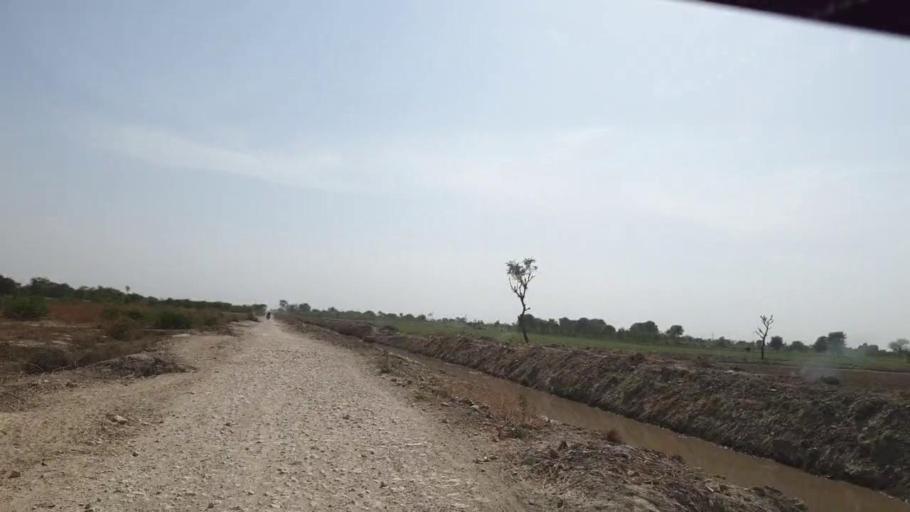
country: PK
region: Sindh
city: Nabisar
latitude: 25.0821
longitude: 69.5801
